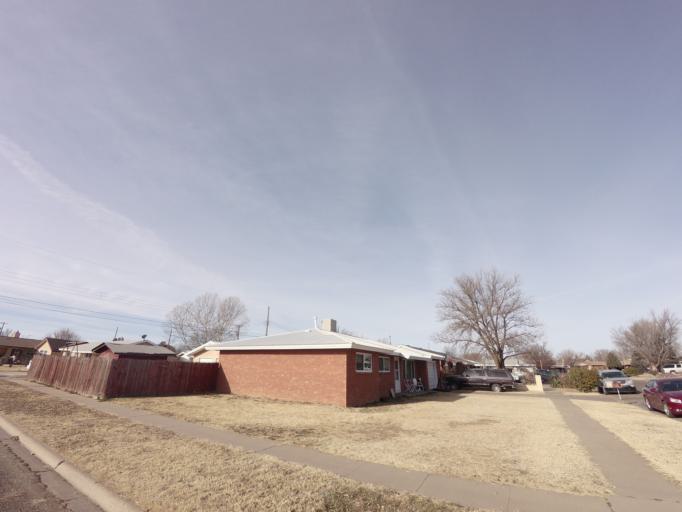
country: US
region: New Mexico
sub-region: Curry County
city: Clovis
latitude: 34.4173
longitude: -103.2207
